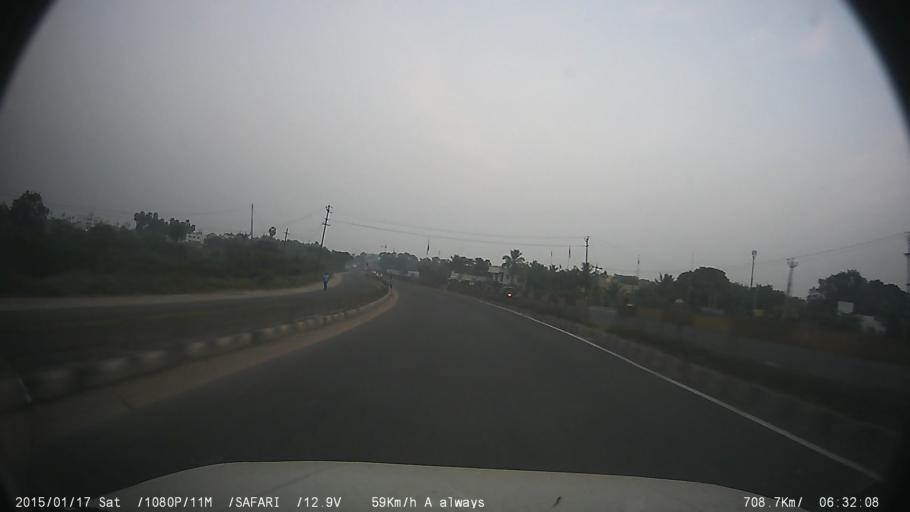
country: IN
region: Tamil Nadu
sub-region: Kancheepuram
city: Sriperumbudur
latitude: 12.9570
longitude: 79.9432
